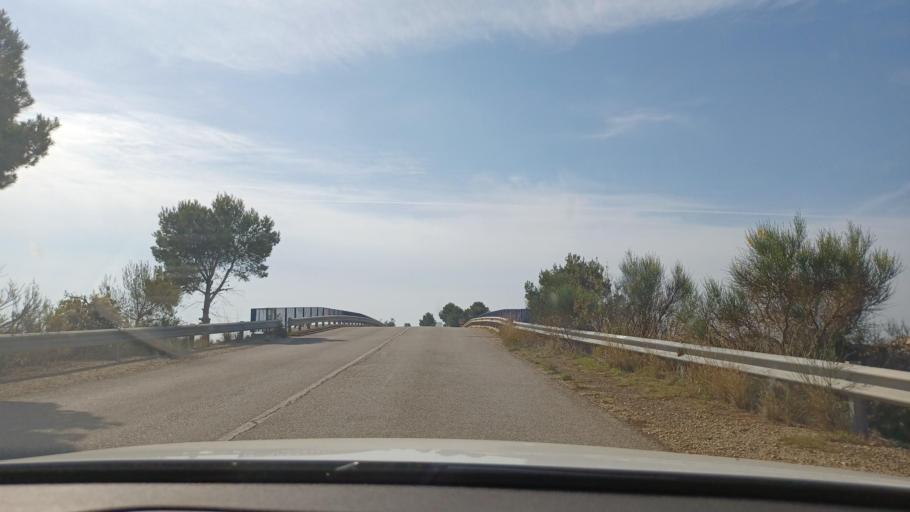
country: ES
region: Catalonia
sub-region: Provincia de Tarragona
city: L'Ampolla
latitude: 40.8190
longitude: 0.7166
